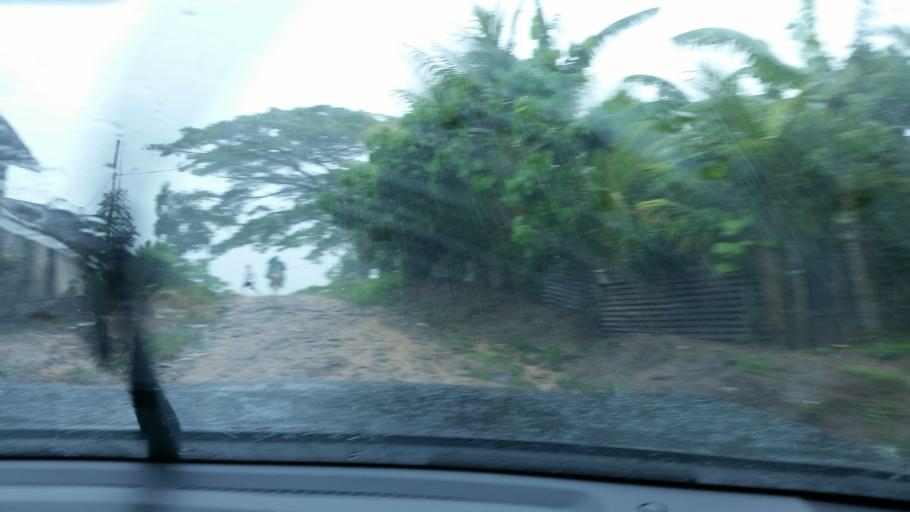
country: NI
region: Atlantico Norte (RAAN)
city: Waslala
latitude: 13.1564
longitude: -85.4364
